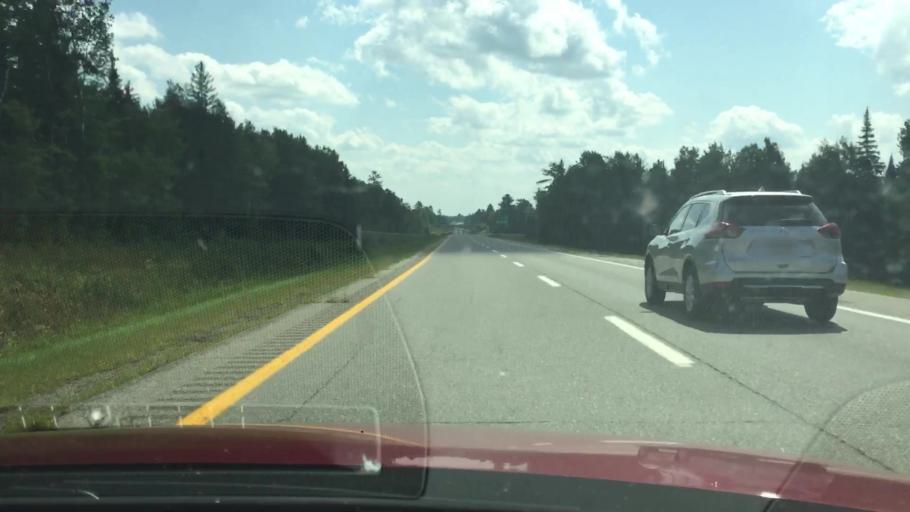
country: US
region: Maine
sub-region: Penobscot County
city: Lincoln
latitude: 45.3838
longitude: -68.6053
